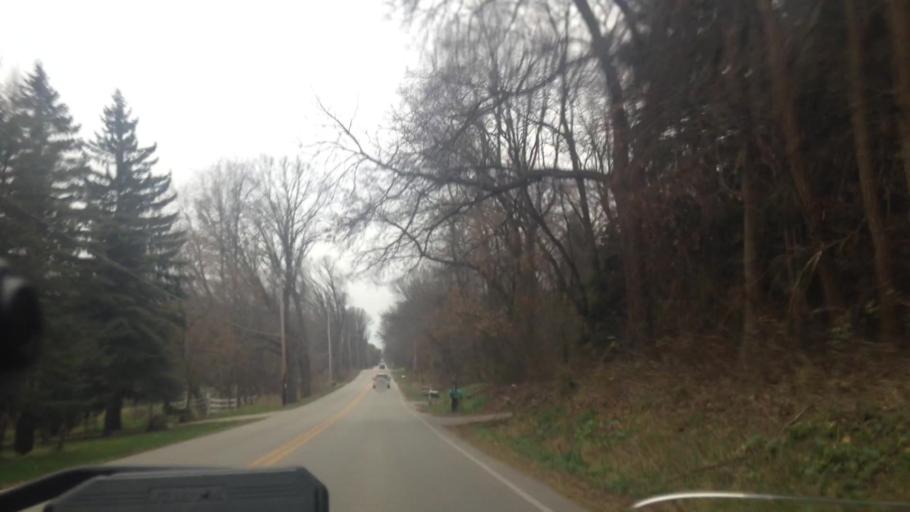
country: US
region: Wisconsin
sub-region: Waukesha County
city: Lannon
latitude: 43.1759
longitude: -88.1829
